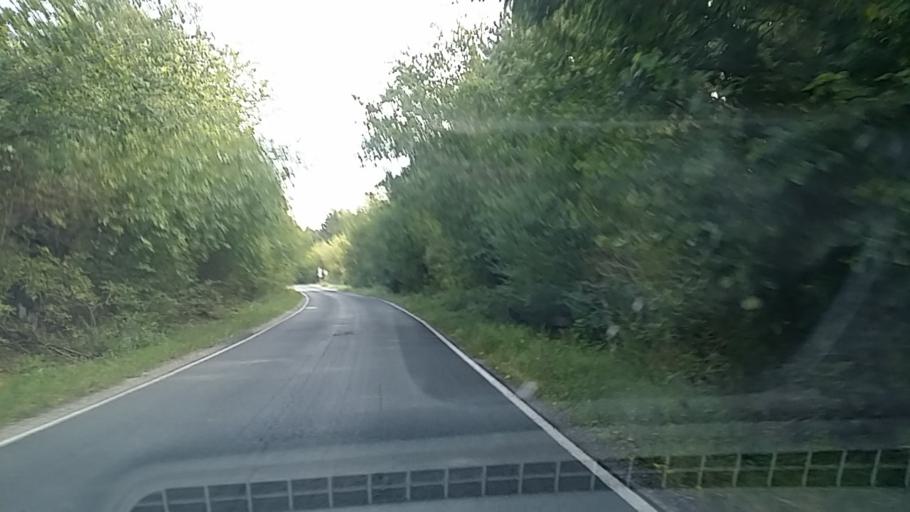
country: HU
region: Gyor-Moson-Sopron
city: Fertorakos
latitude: 47.7321
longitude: 16.6204
